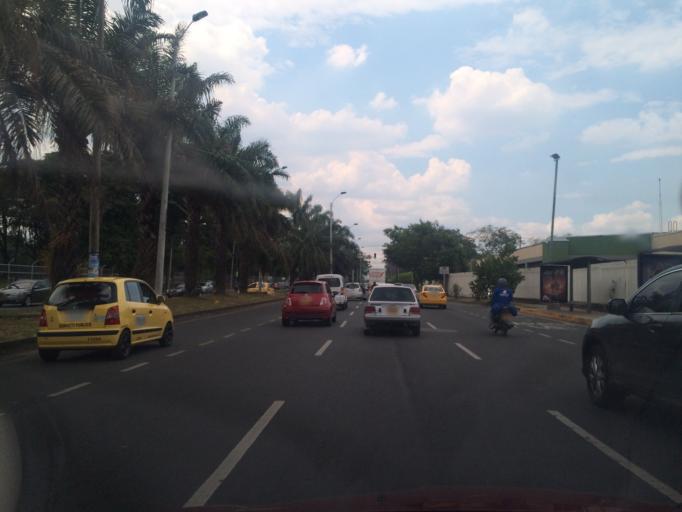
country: CO
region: Valle del Cauca
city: Cali
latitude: 3.3697
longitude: -76.5295
